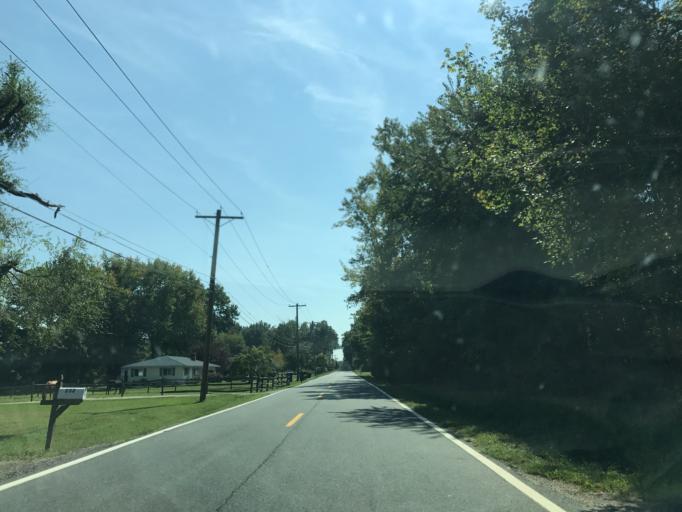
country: US
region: Maryland
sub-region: Cecil County
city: Elkton
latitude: 39.5156
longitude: -75.8134
